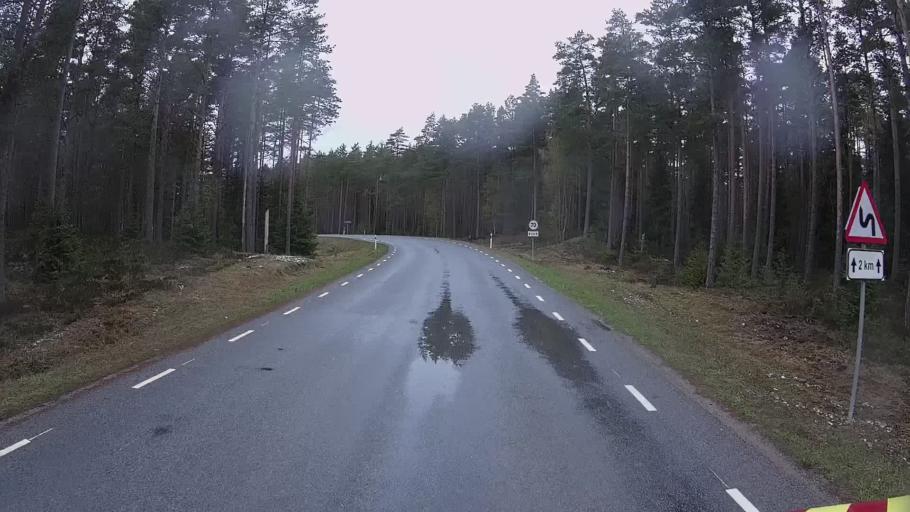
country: EE
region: Hiiumaa
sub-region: Kaerdla linn
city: Kardla
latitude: 58.9086
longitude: 22.3952
